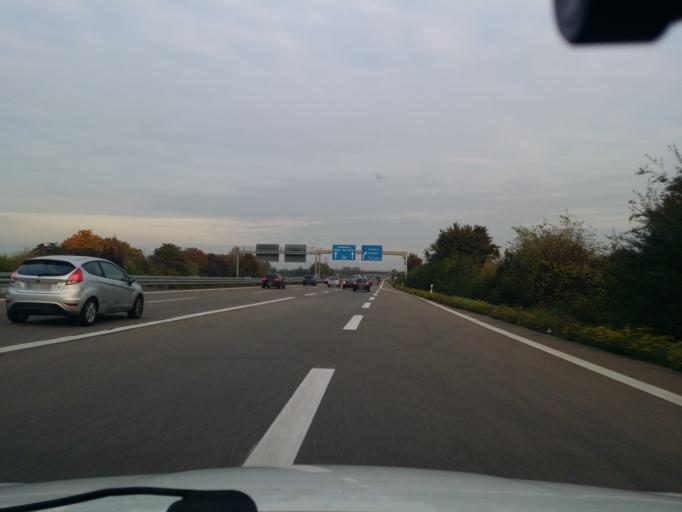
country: DE
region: Rheinland-Pfalz
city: Altrip
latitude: 49.4660
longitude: 8.5231
